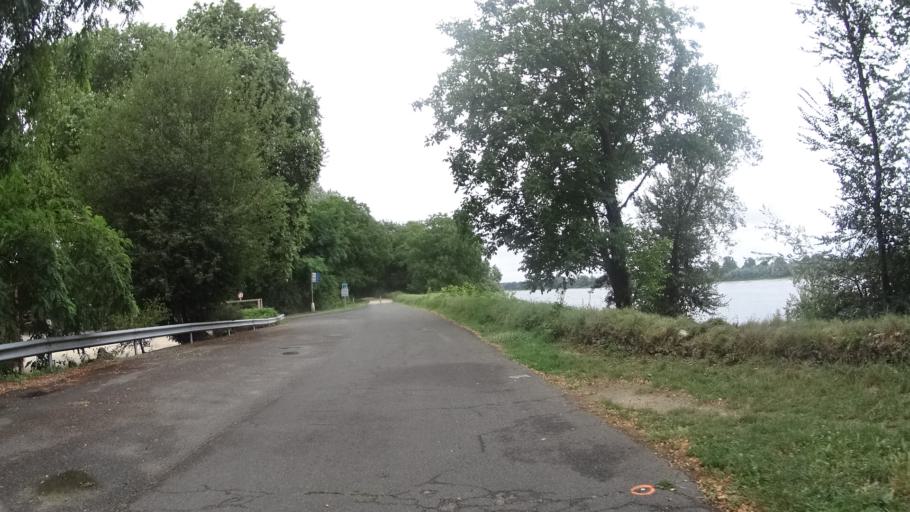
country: FR
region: Centre
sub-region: Departement du Loir-et-Cher
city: La Chaussee-Saint-Victor
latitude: 47.6209
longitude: 1.3886
